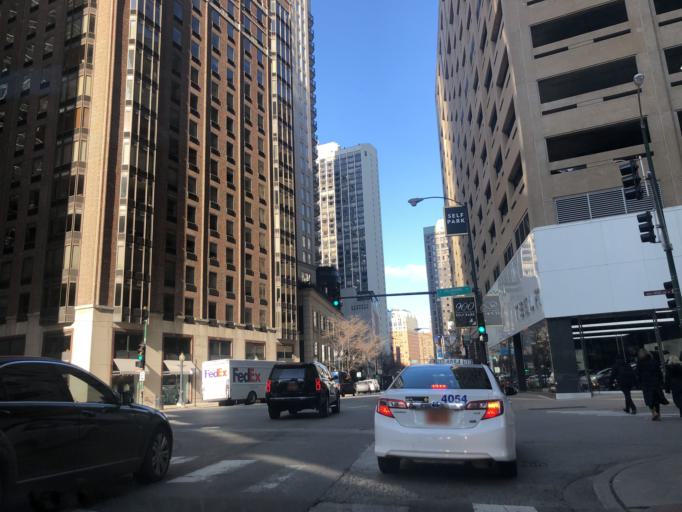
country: US
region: Illinois
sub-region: Cook County
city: Chicago
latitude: 41.8991
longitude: -87.6266
